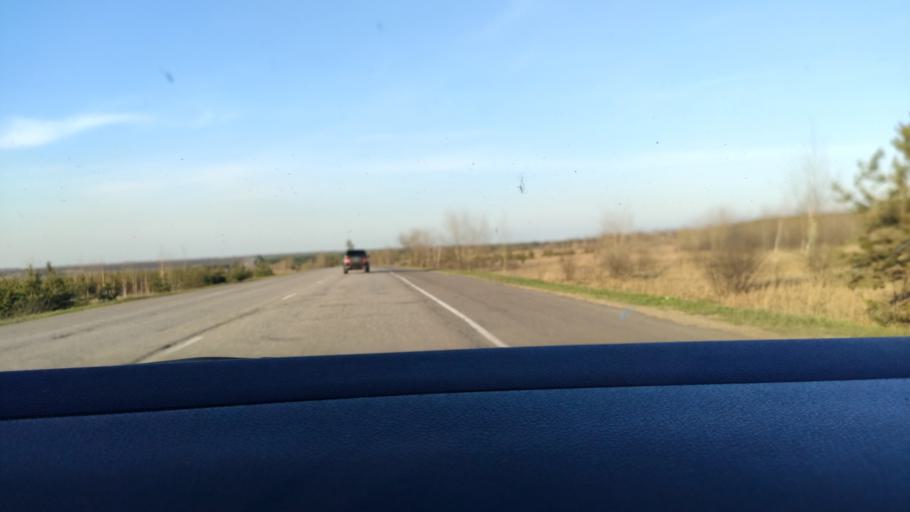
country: RU
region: Voronezj
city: Kolodeznyy
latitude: 51.3715
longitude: 39.2068
